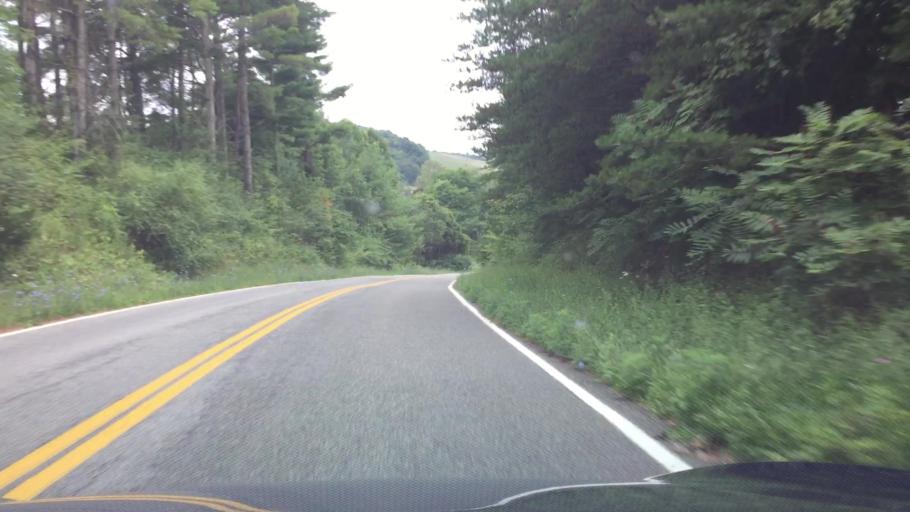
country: US
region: Virginia
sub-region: Pulaski County
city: Pulaski
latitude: 37.0035
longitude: -80.7586
